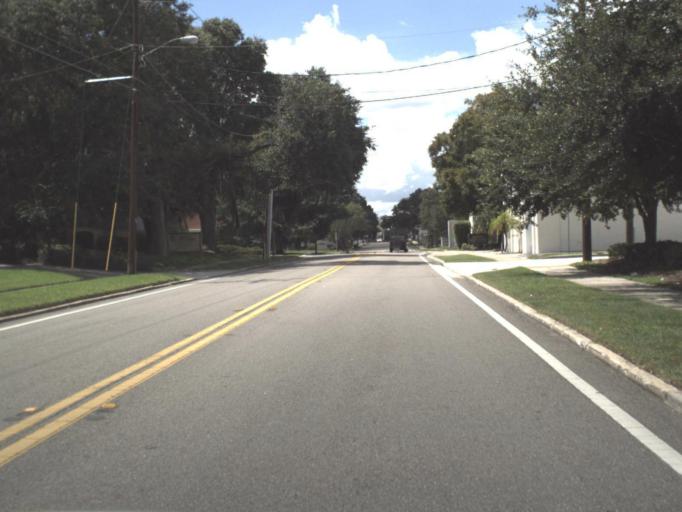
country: US
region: Florida
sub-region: Polk County
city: Winter Haven
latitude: 28.0223
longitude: -81.7217
